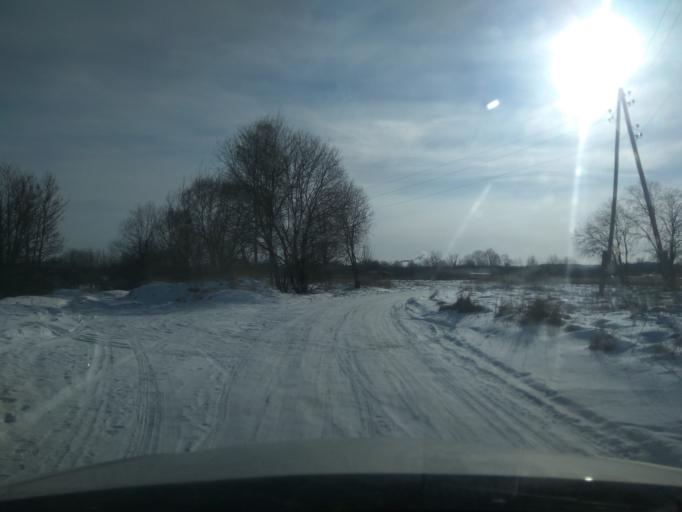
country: LV
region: Kuldigas Rajons
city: Kuldiga
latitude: 56.9846
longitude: 21.9544
